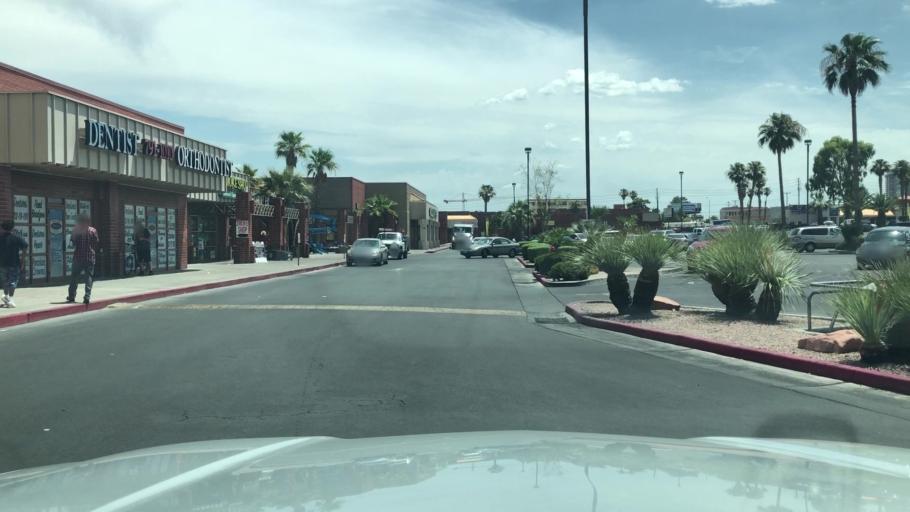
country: US
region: Nevada
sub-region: Clark County
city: Winchester
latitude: 36.1431
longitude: -115.1354
